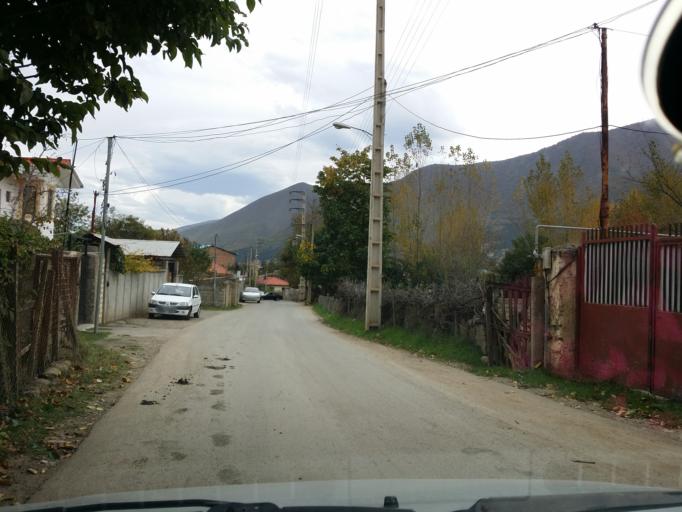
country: IR
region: Mazandaran
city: `Abbasabad
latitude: 36.5046
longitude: 51.1465
